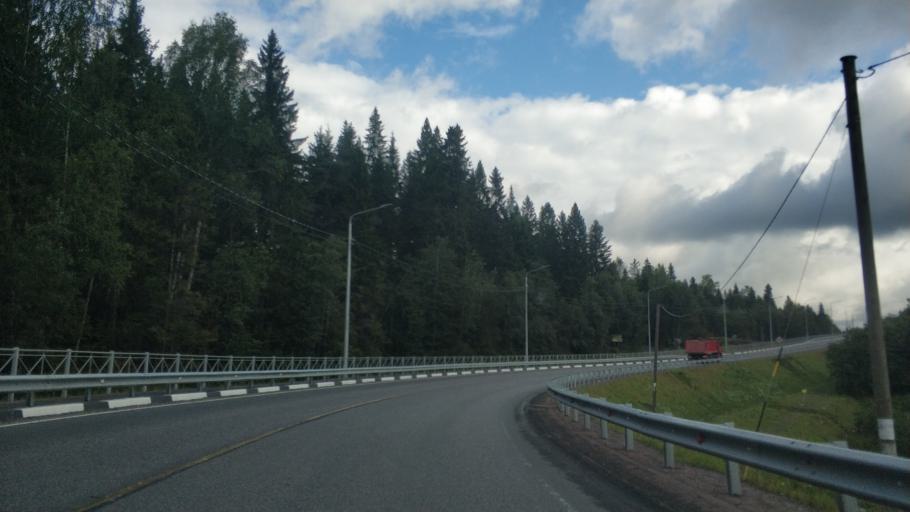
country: RU
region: Republic of Karelia
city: Ruskeala
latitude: 61.9404
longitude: 30.5913
